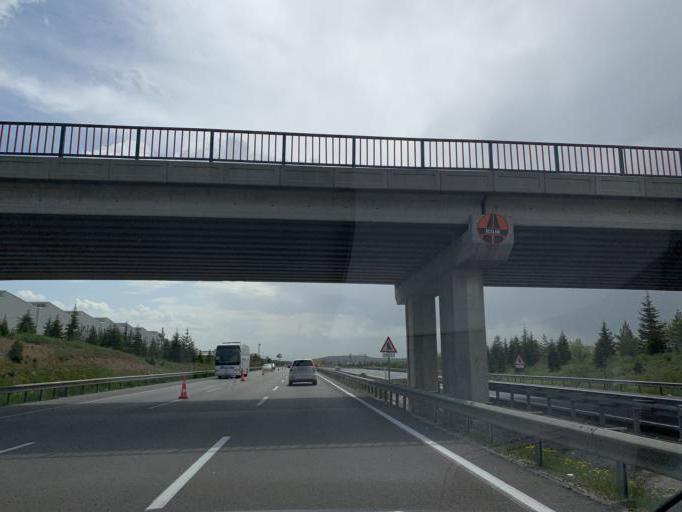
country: TR
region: Ankara
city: Polatli
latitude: 39.6514
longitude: 32.2143
